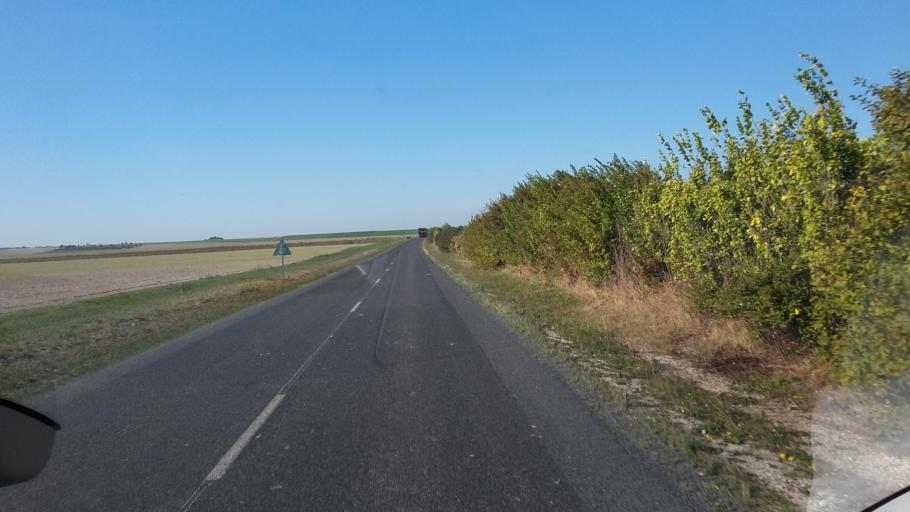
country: FR
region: Champagne-Ardenne
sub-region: Departement de la Marne
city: Connantre
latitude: 48.7463
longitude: 3.8897
